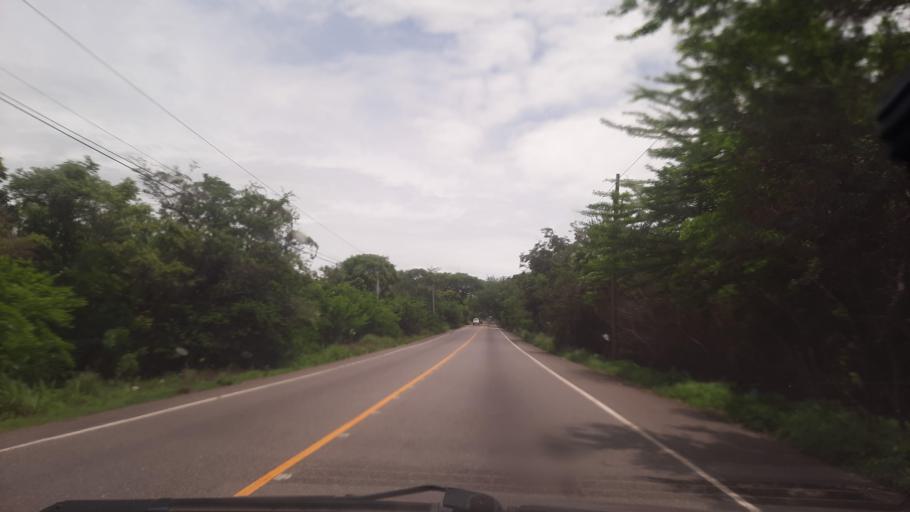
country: GT
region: Zacapa
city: Rio Hondo
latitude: 15.0556
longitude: -89.5538
